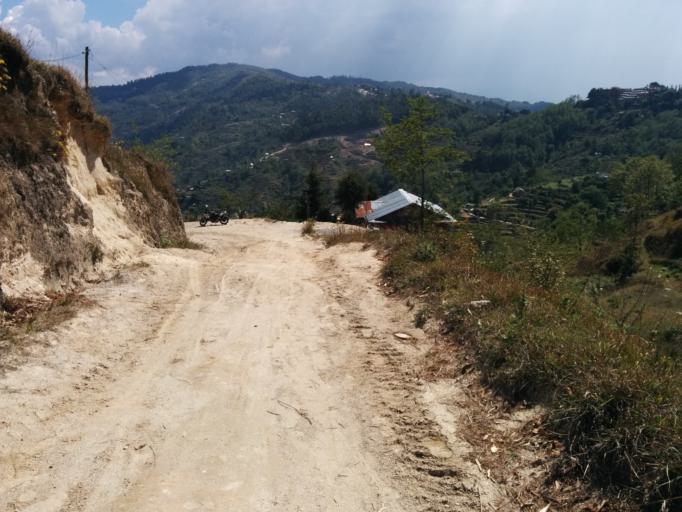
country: NP
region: Central Region
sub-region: Bagmati Zone
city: Nagarkot
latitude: 27.7225
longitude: 85.5276
